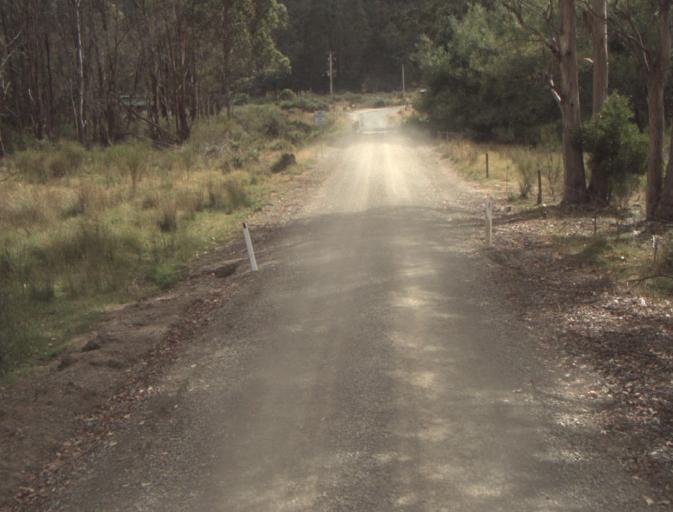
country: AU
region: Tasmania
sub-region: Northern Midlands
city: Evandale
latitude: -41.4508
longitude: 147.4776
